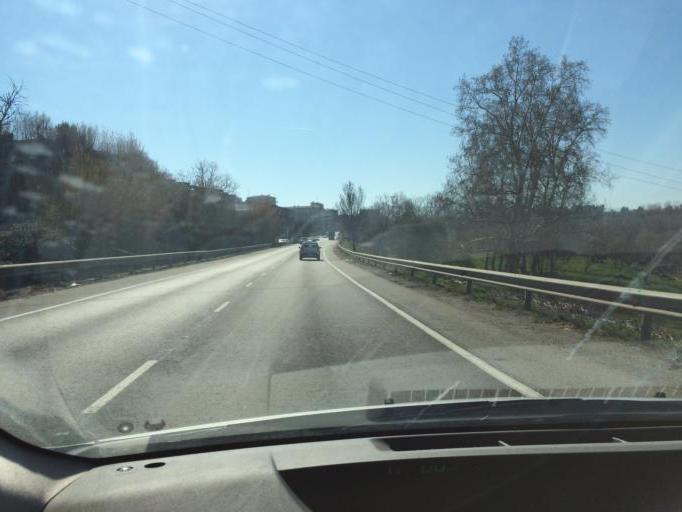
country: ES
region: Catalonia
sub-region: Provincia de Barcelona
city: Manresa
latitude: 41.7309
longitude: 1.8139
